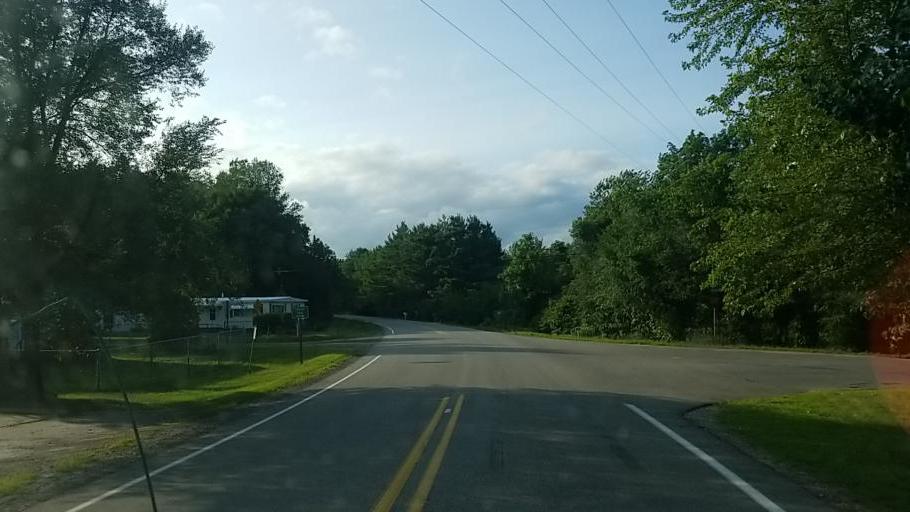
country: US
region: Michigan
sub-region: Montcalm County
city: Greenville
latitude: 43.2440
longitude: -85.3694
